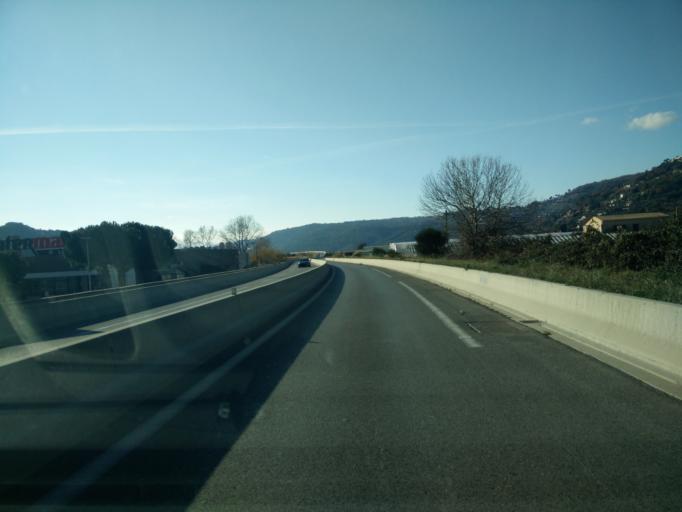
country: FR
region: Provence-Alpes-Cote d'Azur
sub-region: Departement des Alpes-Maritimes
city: Gattieres
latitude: 43.7642
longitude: 7.1991
